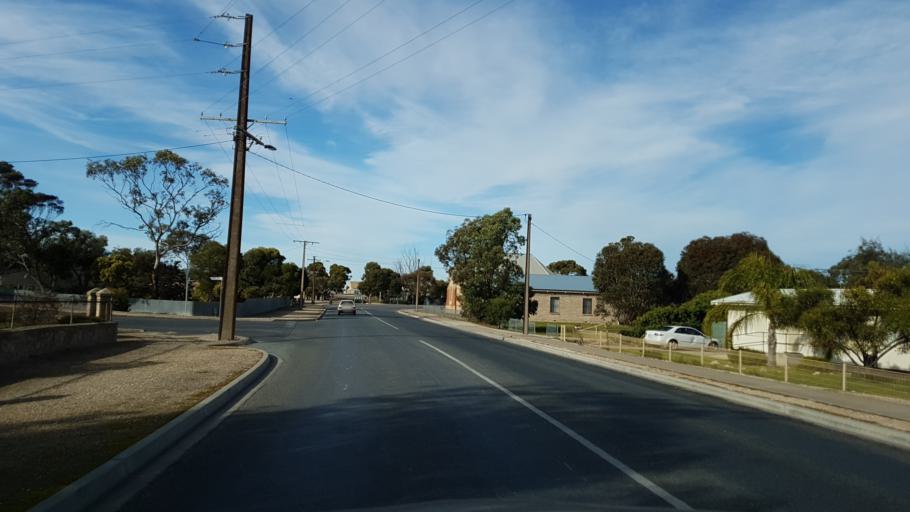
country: AU
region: South Australia
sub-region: Murray Bridge
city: Tailem Bend
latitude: -35.2504
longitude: 139.4553
